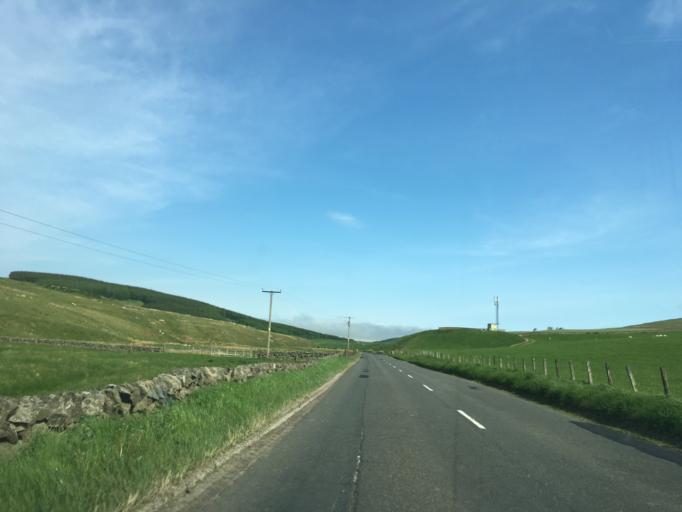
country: GB
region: Scotland
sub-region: South Lanarkshire
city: Biggar
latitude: 55.6292
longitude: -3.4182
